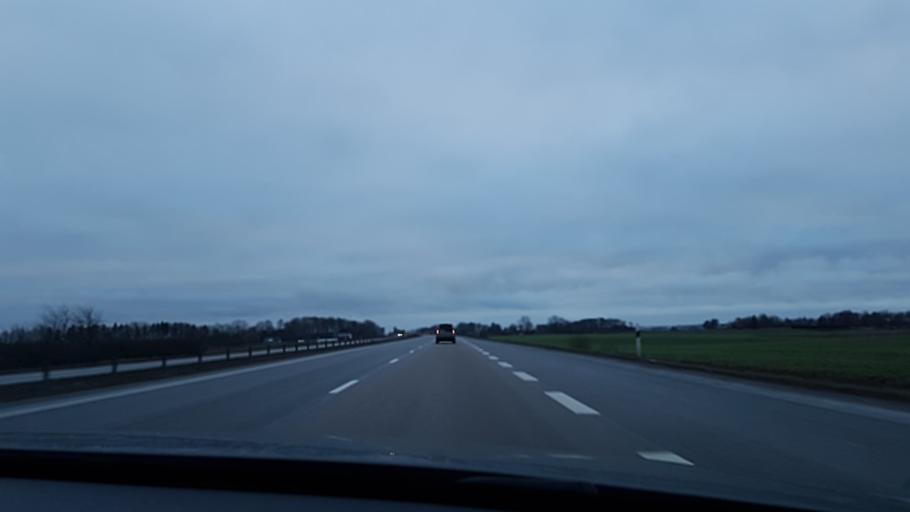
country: SE
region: Skane
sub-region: Astorps Kommun
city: Kvidinge
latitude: 56.1899
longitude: 13.0510
